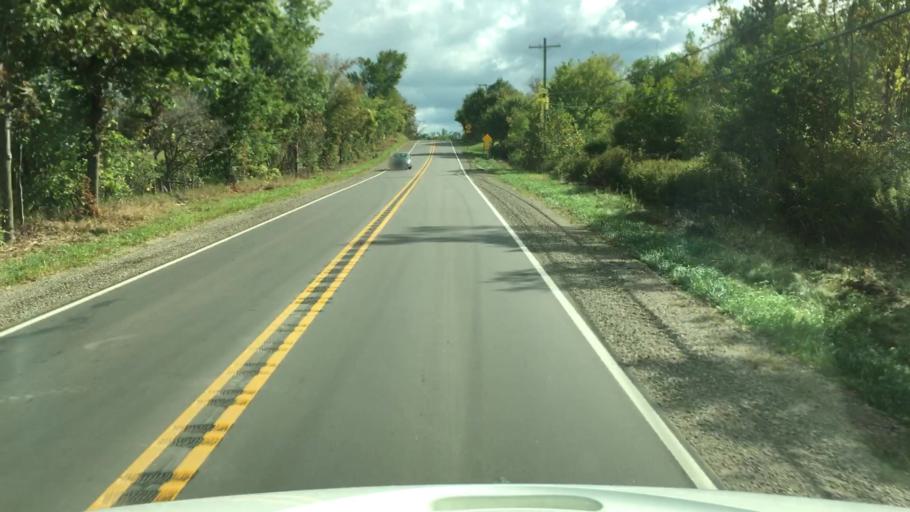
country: US
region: Michigan
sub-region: Oakland County
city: Oxford
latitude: 42.8683
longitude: -83.3234
